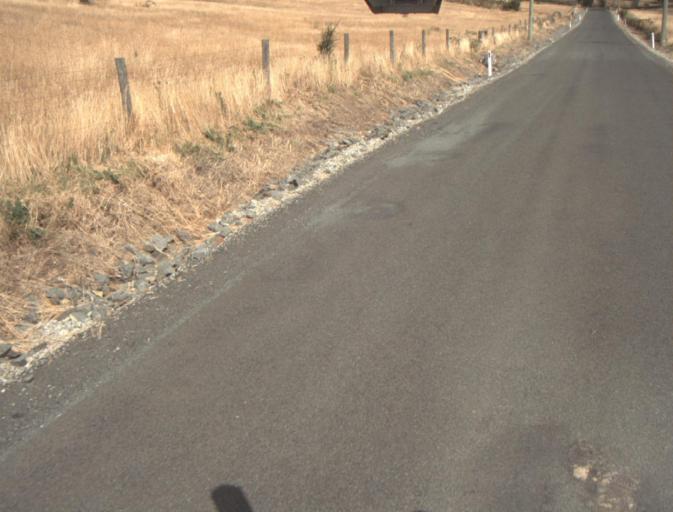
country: AU
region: Tasmania
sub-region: Launceston
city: Mayfield
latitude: -41.3101
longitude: 146.9953
